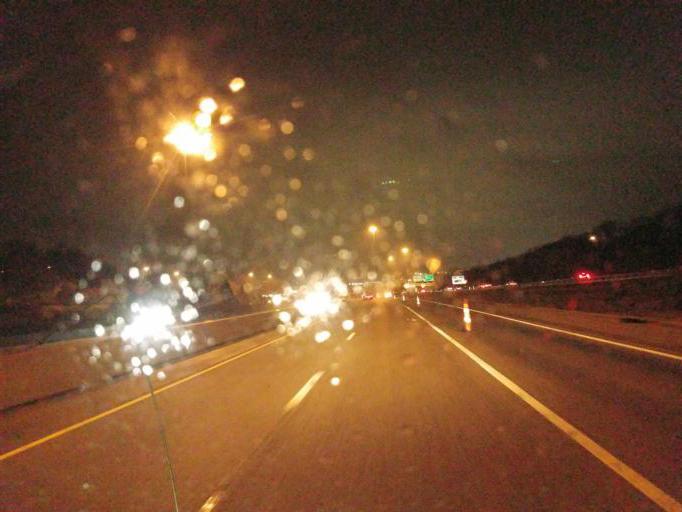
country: US
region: Missouri
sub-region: Saint Louis County
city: Sunset Hills
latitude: 38.5524
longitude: -90.4220
